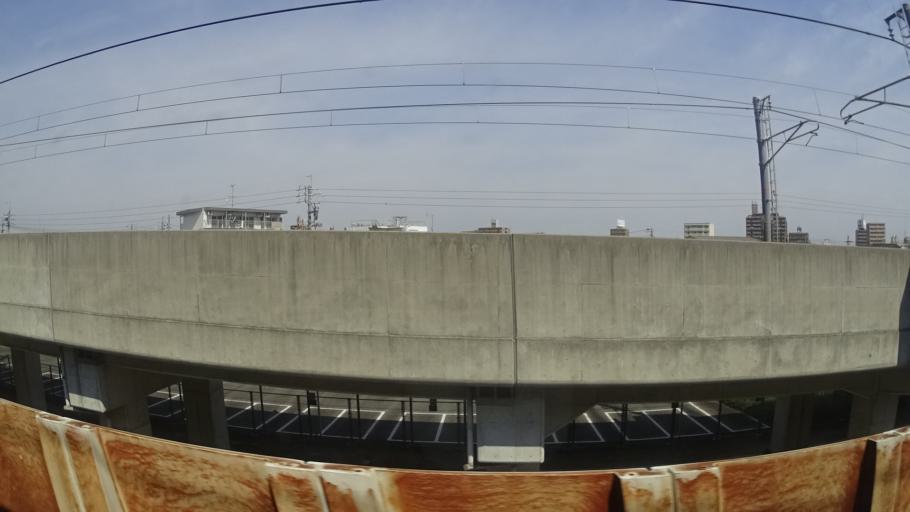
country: JP
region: Aichi
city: Nagoya-shi
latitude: 35.1533
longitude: 136.8648
